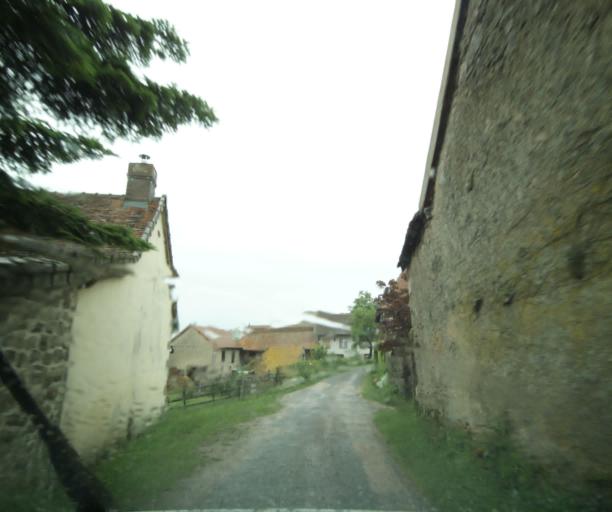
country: FR
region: Bourgogne
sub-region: Departement de Saone-et-Loire
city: Matour
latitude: 46.4333
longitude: 4.4706
